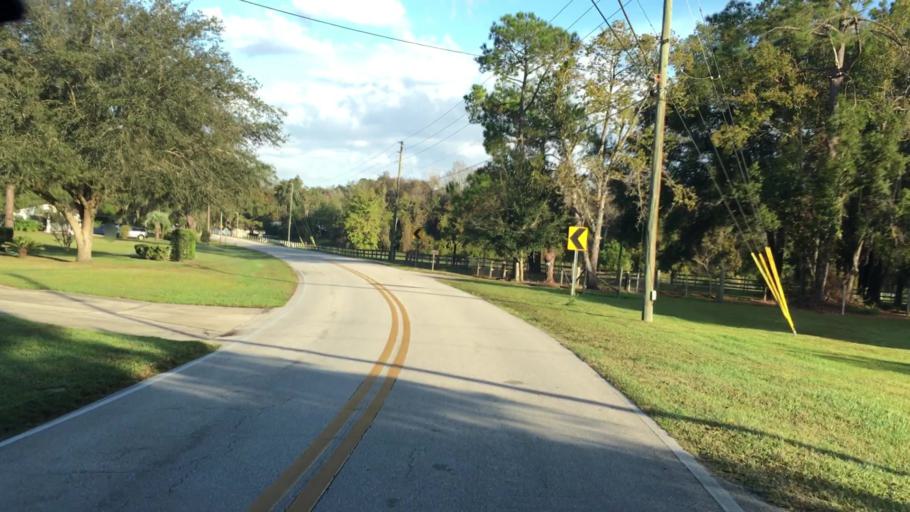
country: US
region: Florida
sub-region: Volusia County
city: North DeLand
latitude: 29.0733
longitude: -81.2713
